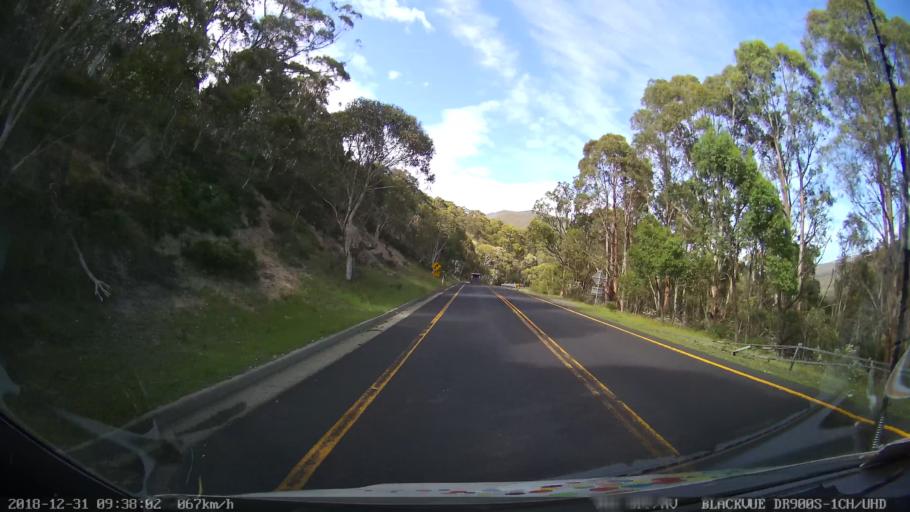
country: AU
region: New South Wales
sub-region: Snowy River
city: Jindabyne
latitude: -36.4714
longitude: 148.3712
